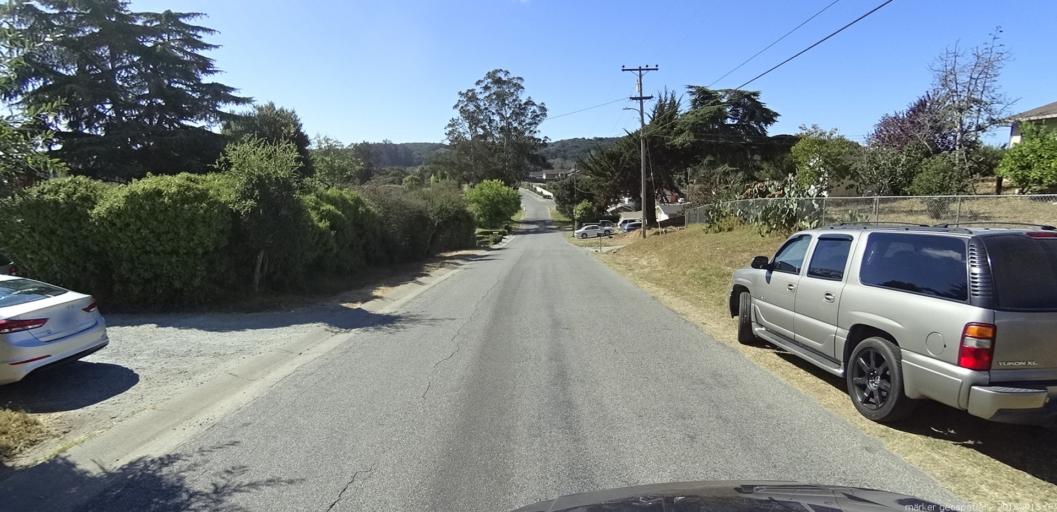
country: US
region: California
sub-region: Monterey County
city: Las Lomas
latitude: 36.8693
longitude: -121.7308
